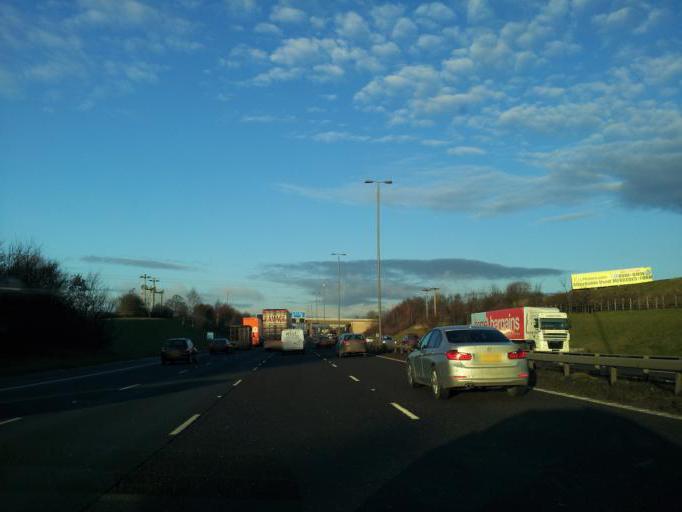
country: GB
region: England
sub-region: City and Borough of Leeds
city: Morley
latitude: 53.7333
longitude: -1.5567
